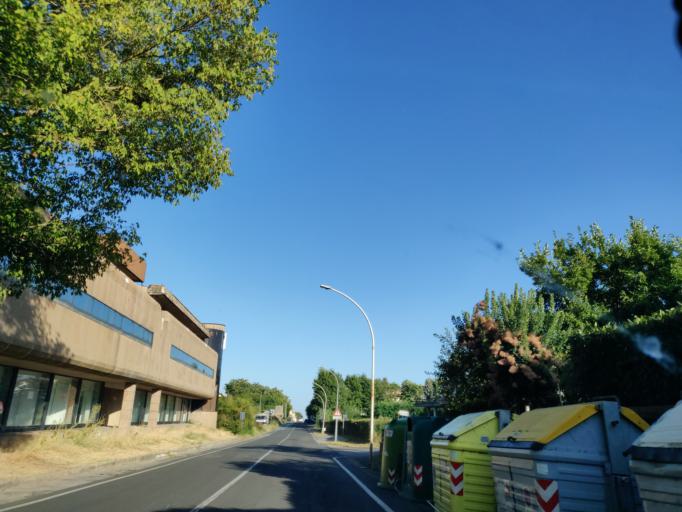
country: IT
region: Tuscany
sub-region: Provincia di Siena
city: Piancastagnaio
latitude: 42.8526
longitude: 11.6863
